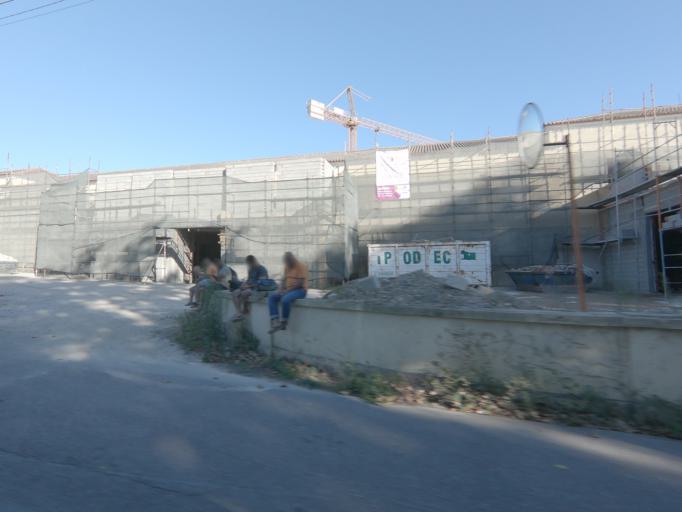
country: PT
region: Setubal
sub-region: Palmela
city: Quinta do Anjo
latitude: 38.5252
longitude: -8.9918
